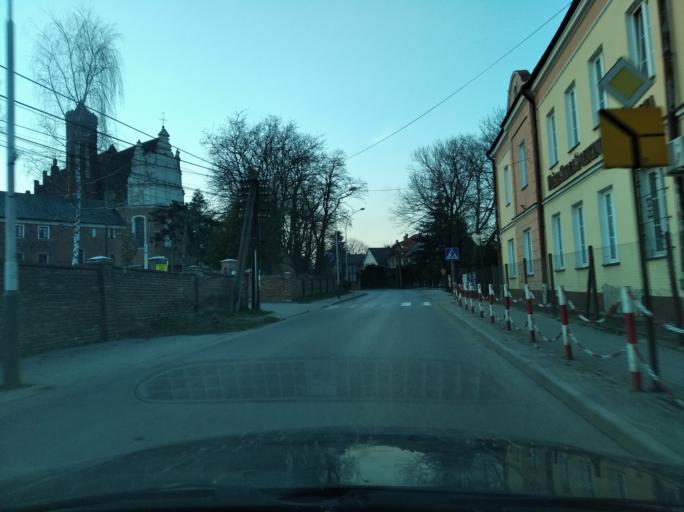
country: PL
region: Subcarpathian Voivodeship
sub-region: Powiat przeworski
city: Przeworsk
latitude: 50.0549
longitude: 22.4999
